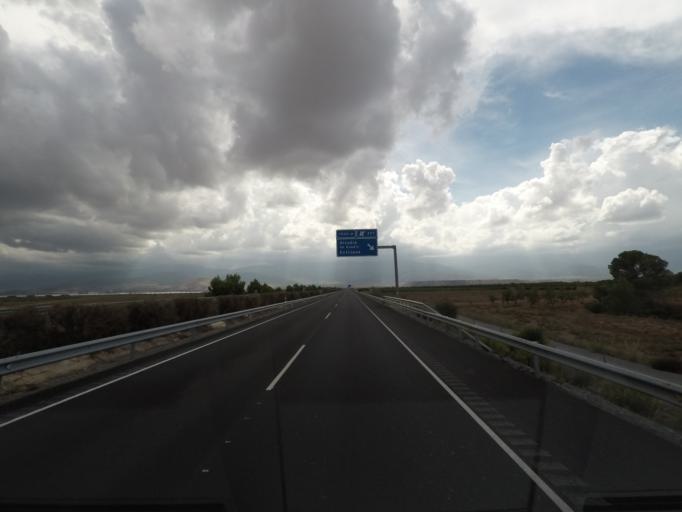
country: ES
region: Andalusia
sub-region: Provincia de Granada
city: Albunan
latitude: 37.2450
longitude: -3.0818
